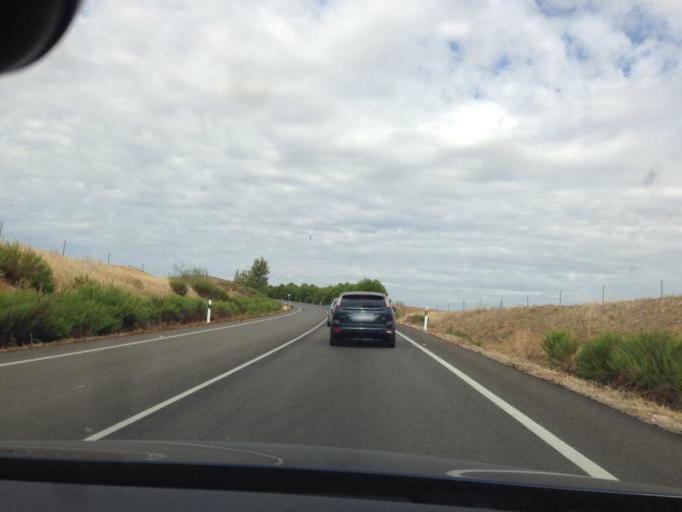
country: ES
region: Madrid
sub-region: Provincia de Madrid
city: Daganzo de Arriba
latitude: 40.5328
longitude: -3.4291
